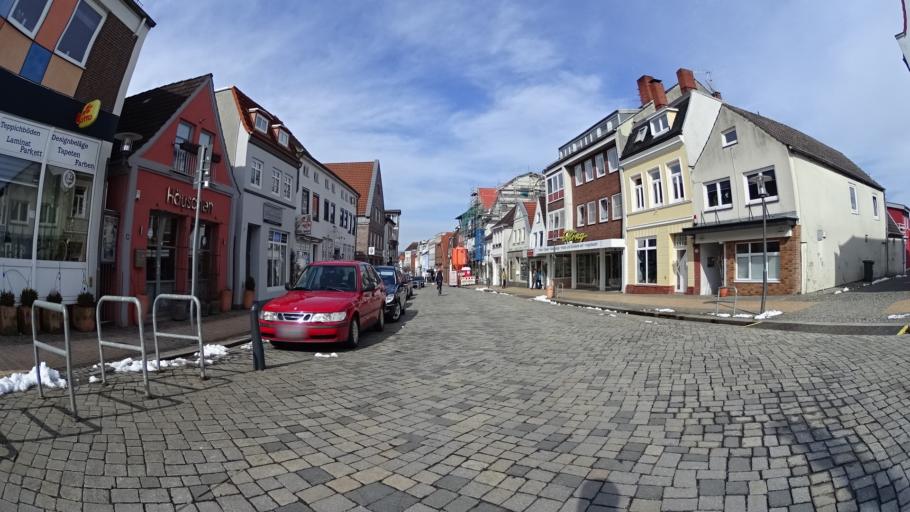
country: DE
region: Schleswig-Holstein
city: Preetz
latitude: 54.2329
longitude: 10.2814
